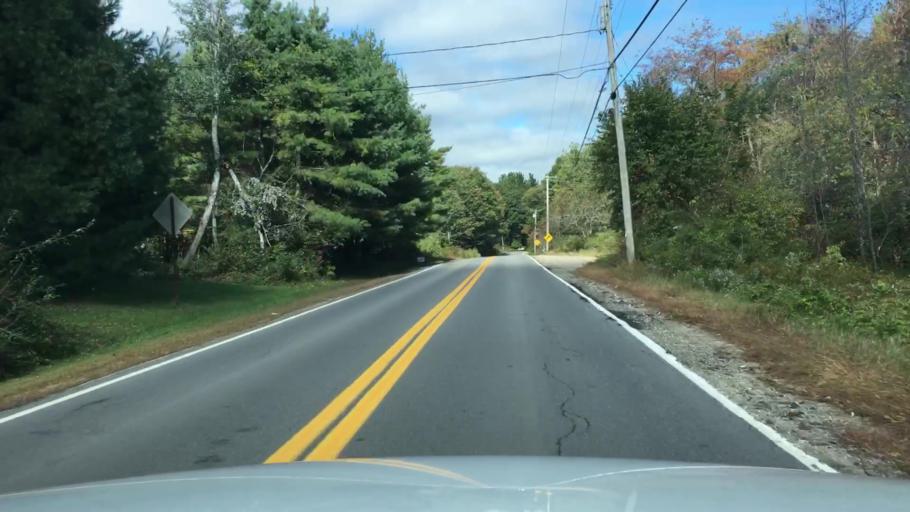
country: US
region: Maine
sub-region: Sagadahoc County
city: North Bath
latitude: 43.9882
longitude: -69.8898
